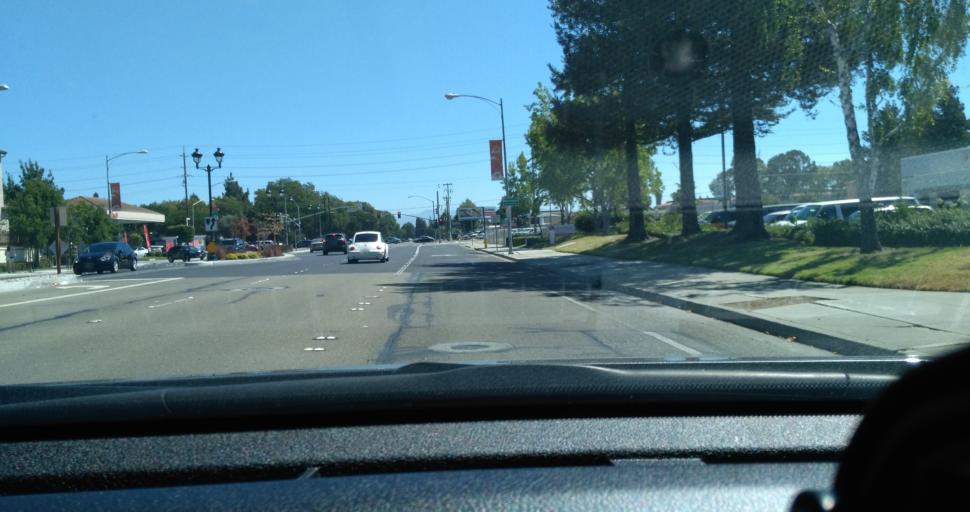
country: US
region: California
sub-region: Santa Clara County
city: Milpitas
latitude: 37.4059
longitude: -121.9031
